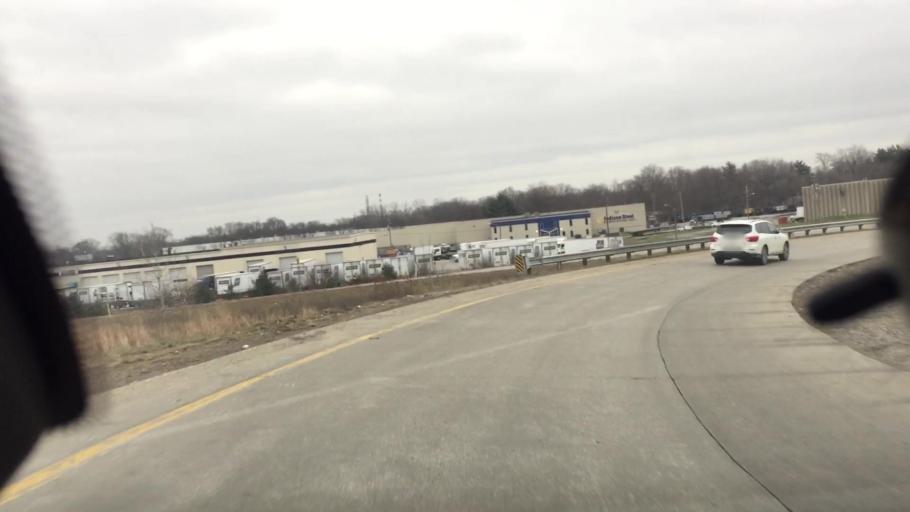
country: US
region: Indiana
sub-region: Marion County
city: Speedway
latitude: 39.7312
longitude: -86.2410
